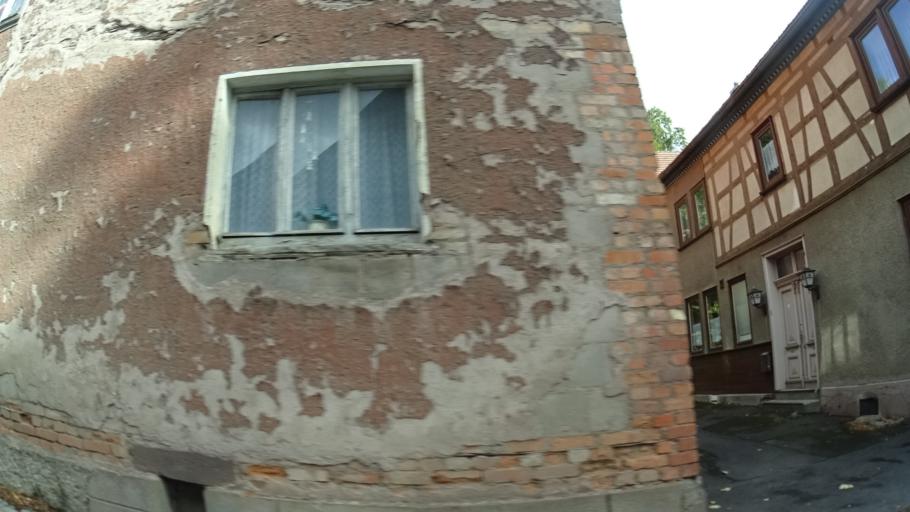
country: DE
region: Thuringia
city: Steinbach-Hallenberg
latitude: 50.7060
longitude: 10.5709
